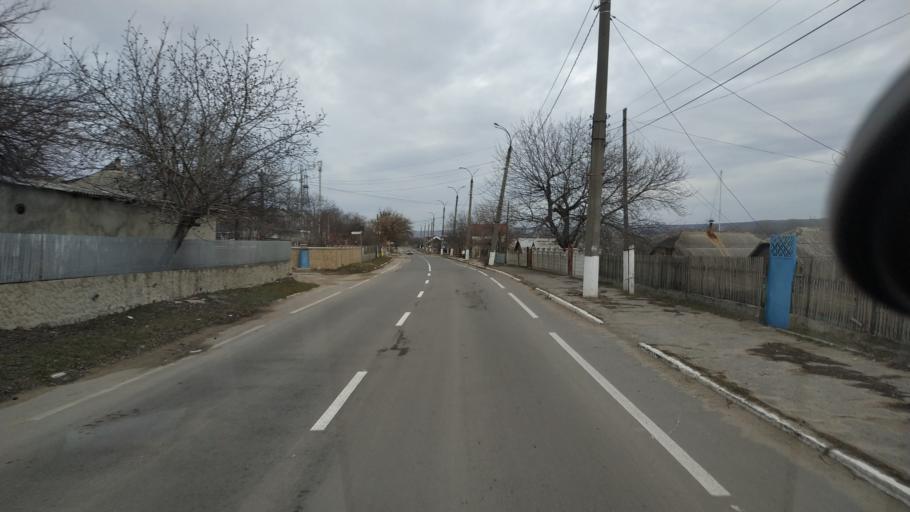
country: MD
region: Criuleni
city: Criuleni
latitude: 47.2211
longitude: 29.1634
